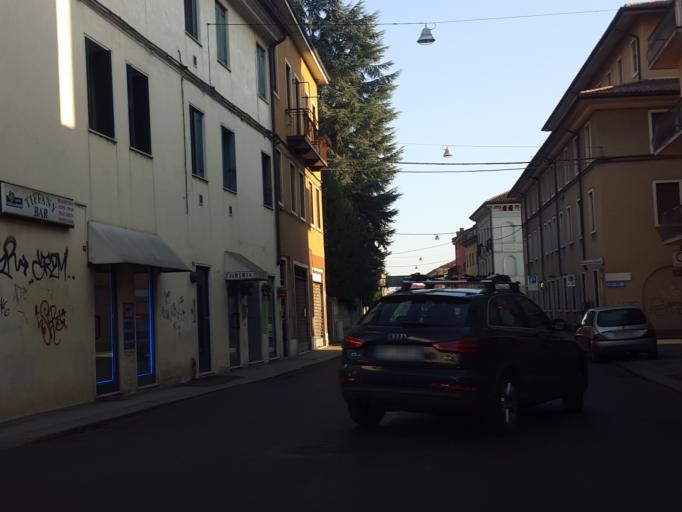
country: IT
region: Veneto
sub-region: Provincia di Vicenza
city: Vicenza
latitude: 45.5479
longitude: 11.5581
